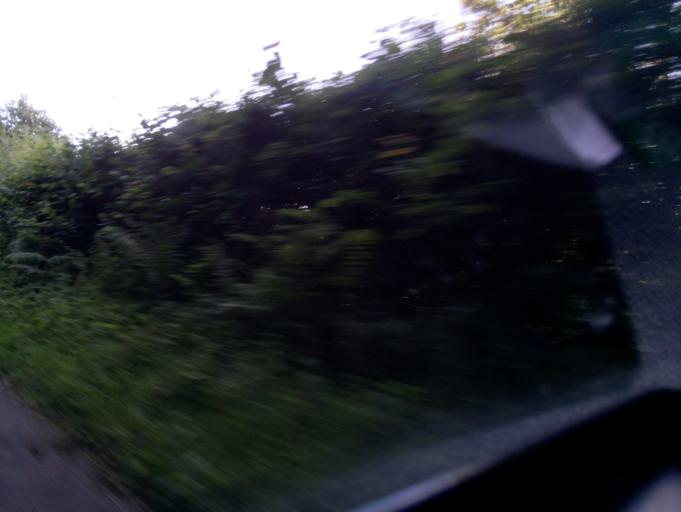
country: GB
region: Wales
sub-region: Monmouthshire
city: Tintern
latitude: 51.6779
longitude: -2.7533
